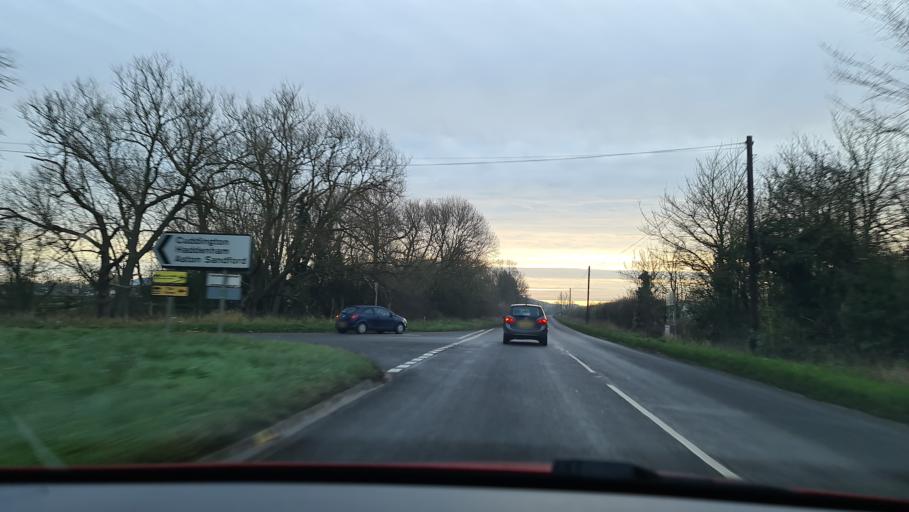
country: GB
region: England
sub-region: Buckinghamshire
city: Haddenham
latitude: 51.7524
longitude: -0.8890
